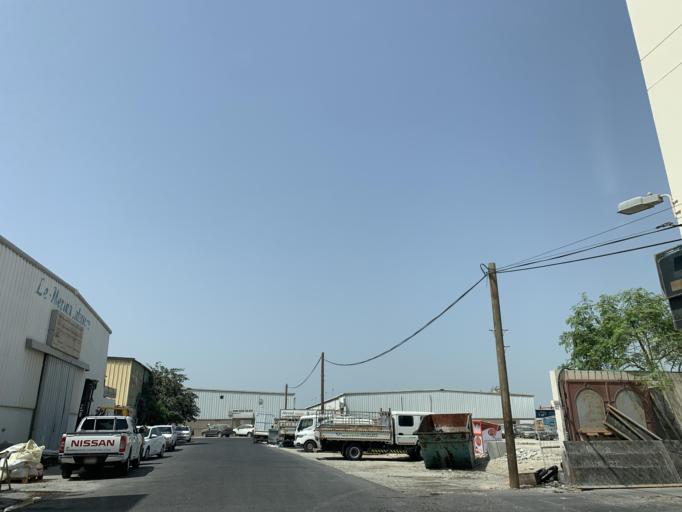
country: BH
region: Northern
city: Madinat `Isa
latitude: 26.1916
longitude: 50.5389
